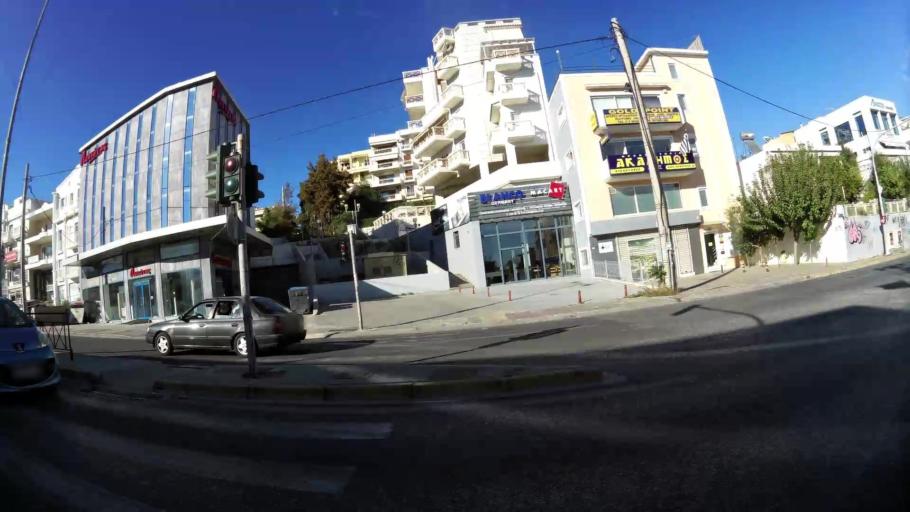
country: GR
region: Attica
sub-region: Nomarchia Anatolikis Attikis
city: Pallini
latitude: 38.0037
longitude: 23.8773
